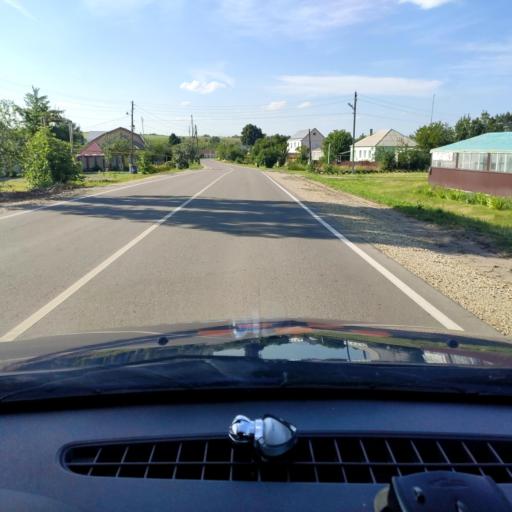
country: RU
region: Voronezj
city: Devitsa
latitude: 51.6533
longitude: 38.9720
